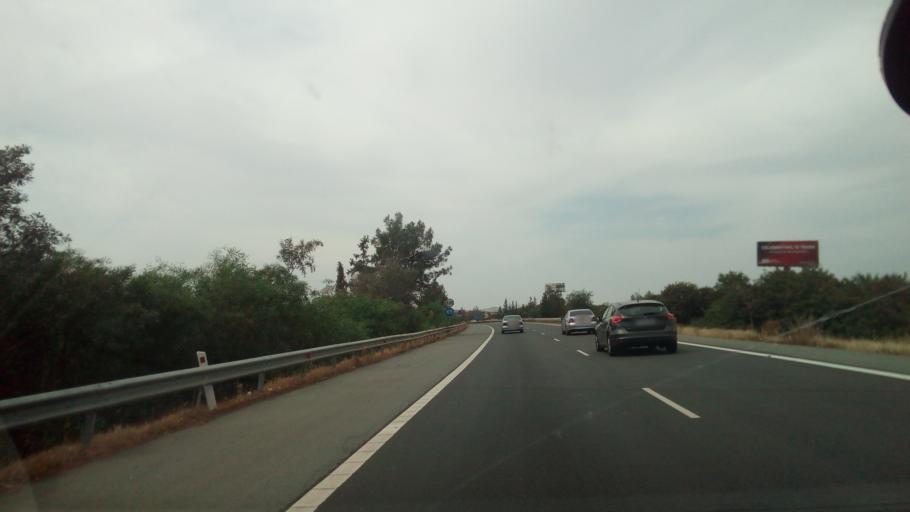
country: CY
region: Larnaka
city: Aradippou
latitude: 34.9575
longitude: 33.5716
